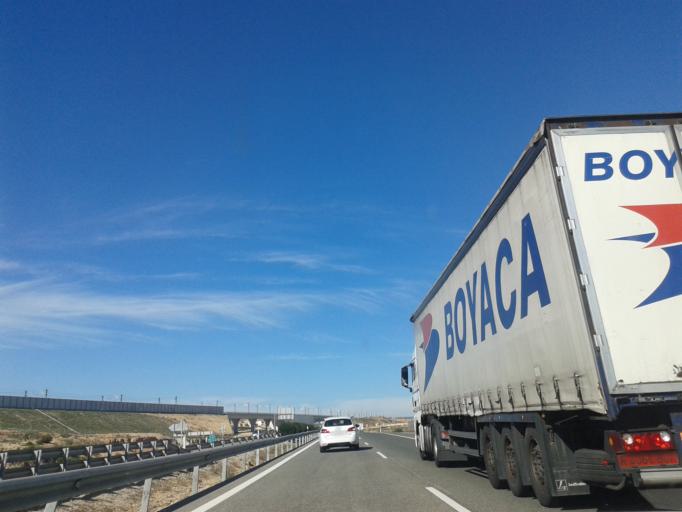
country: ES
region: Castille-La Mancha
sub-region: Provincia de Albacete
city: Caudete
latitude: 38.7147
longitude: -0.9288
